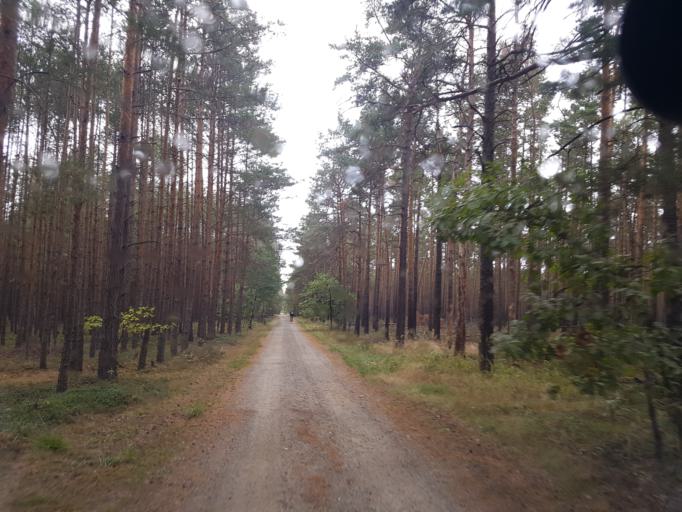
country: DE
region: Brandenburg
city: Sallgast
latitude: 51.6136
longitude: 13.7784
